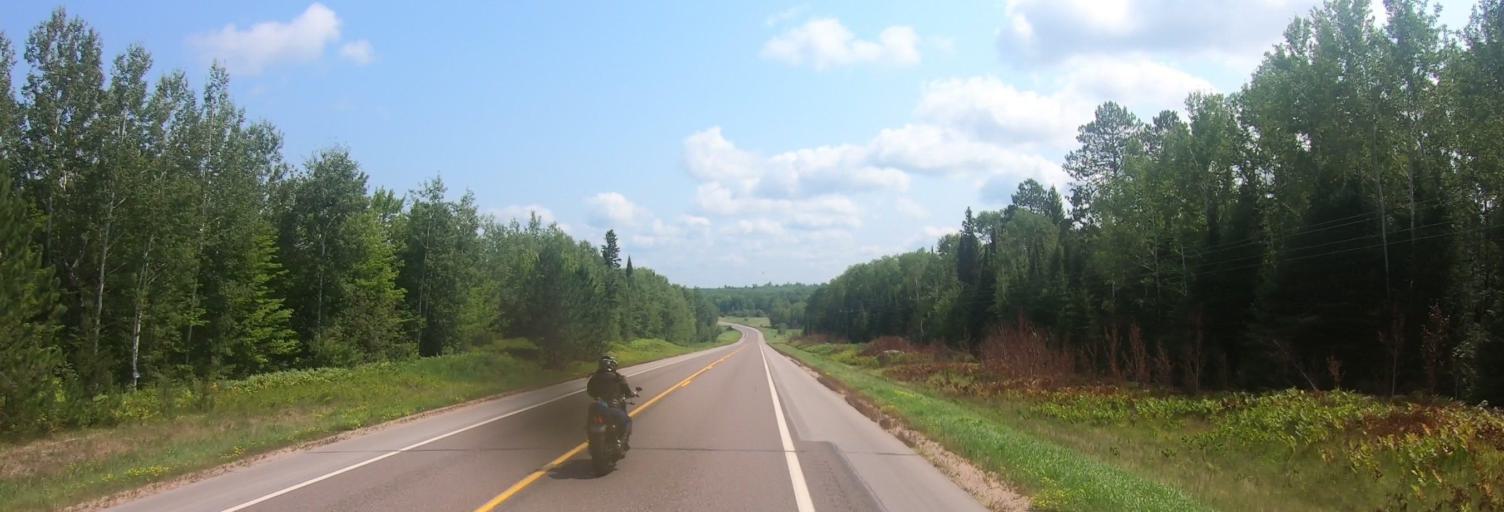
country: US
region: Minnesota
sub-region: Saint Louis County
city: Mountain Iron
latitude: 48.0601
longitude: -92.7427
